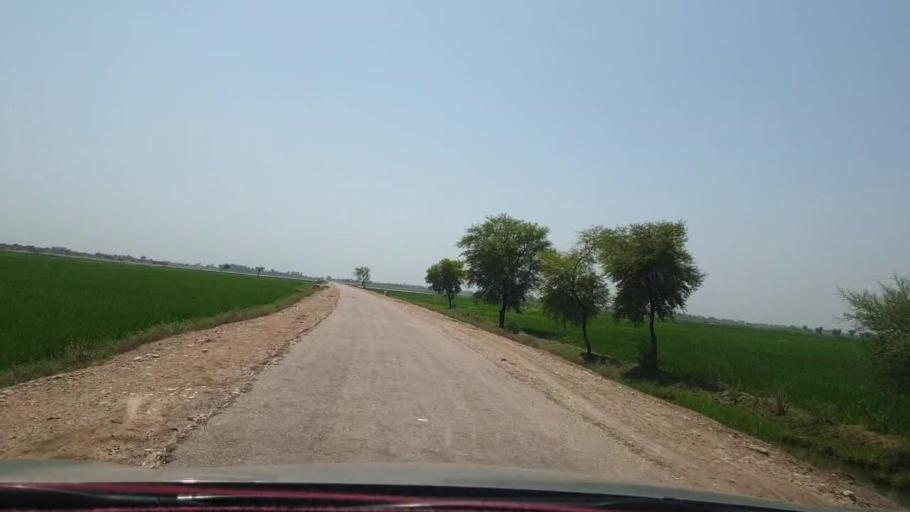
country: PK
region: Sindh
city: Warah
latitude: 27.5546
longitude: 67.7975
